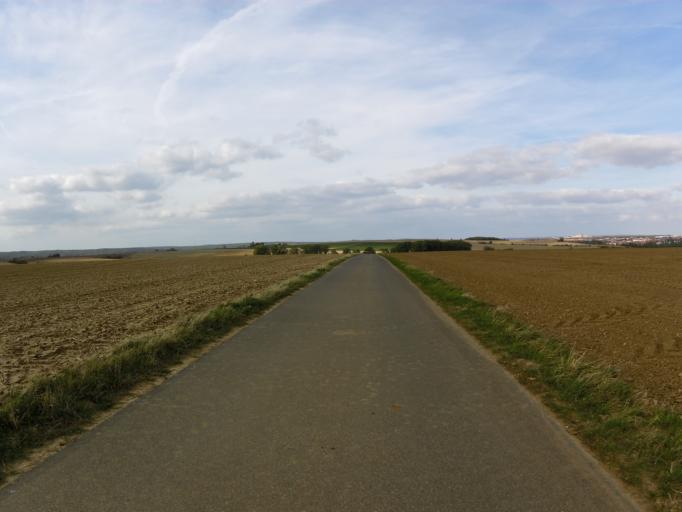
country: DE
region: Bavaria
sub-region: Regierungsbezirk Unterfranken
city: Eibelstadt
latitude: 49.6997
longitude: 9.9579
